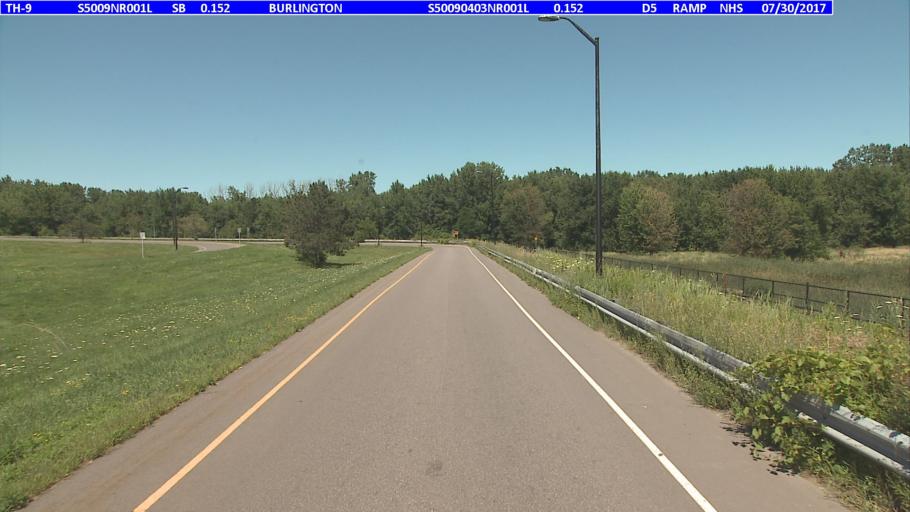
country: US
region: Vermont
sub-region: Chittenden County
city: Burlington
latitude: 44.5006
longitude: -73.2288
